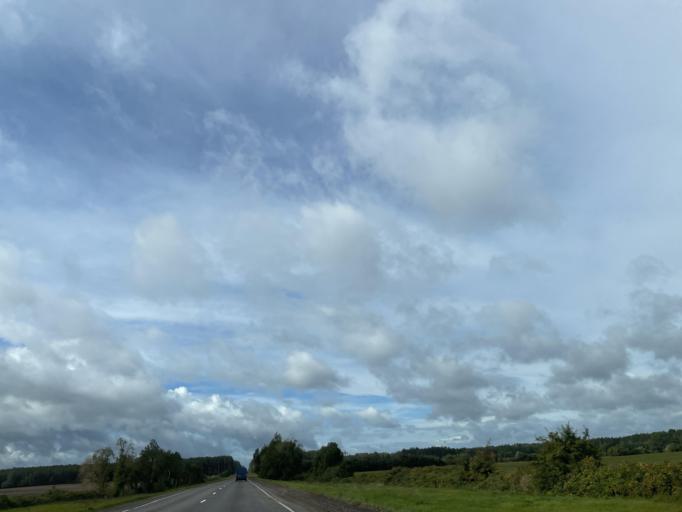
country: BY
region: Brest
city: Ivatsevichy
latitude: 52.7348
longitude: 25.2499
